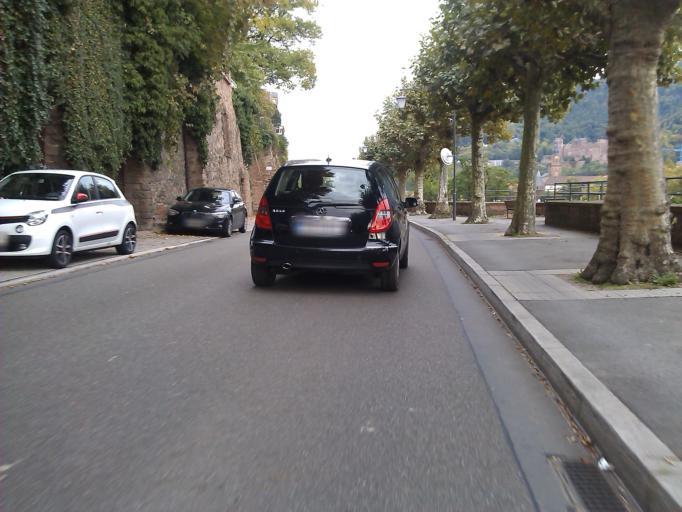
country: DE
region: Baden-Wuerttemberg
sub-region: Karlsruhe Region
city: Heidelberg
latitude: 49.4136
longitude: 8.6979
